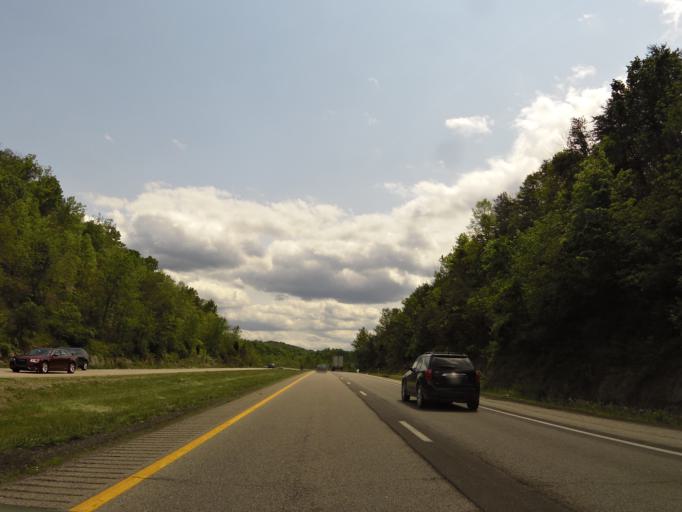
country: US
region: West Virginia
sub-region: Kanawha County
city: Sissonville
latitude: 38.4985
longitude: -81.6434
